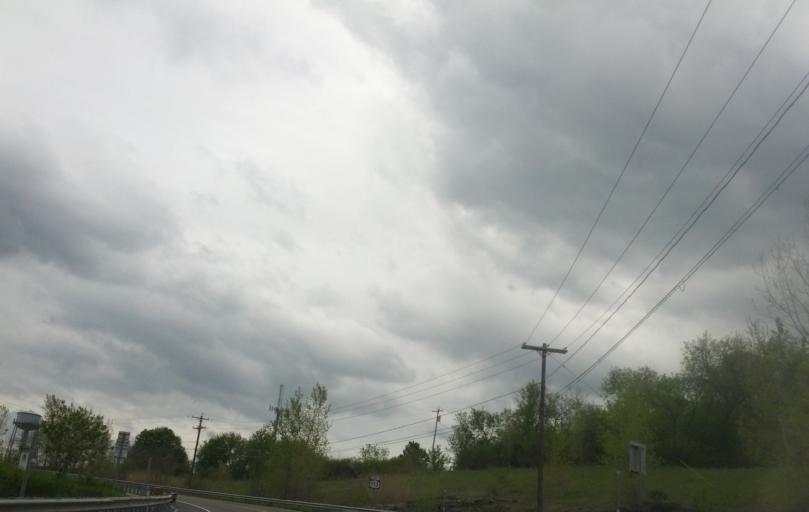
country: US
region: New York
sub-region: Onondaga County
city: Nedrow
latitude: 42.9903
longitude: -76.0685
